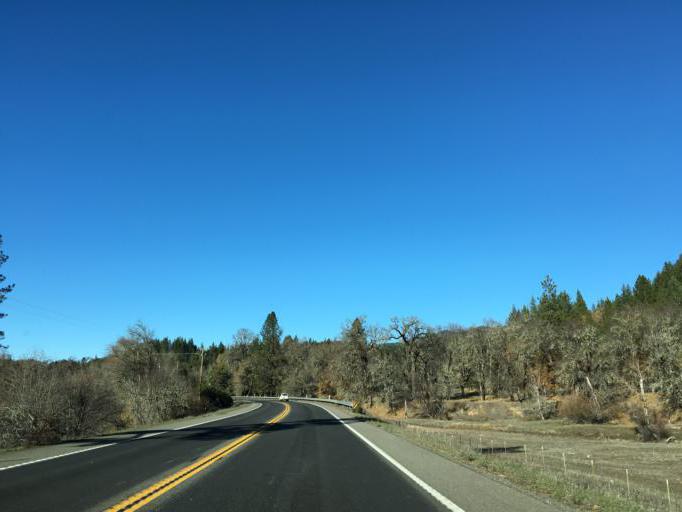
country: US
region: California
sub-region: Mendocino County
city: Laytonville
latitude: 39.7366
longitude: -123.5138
